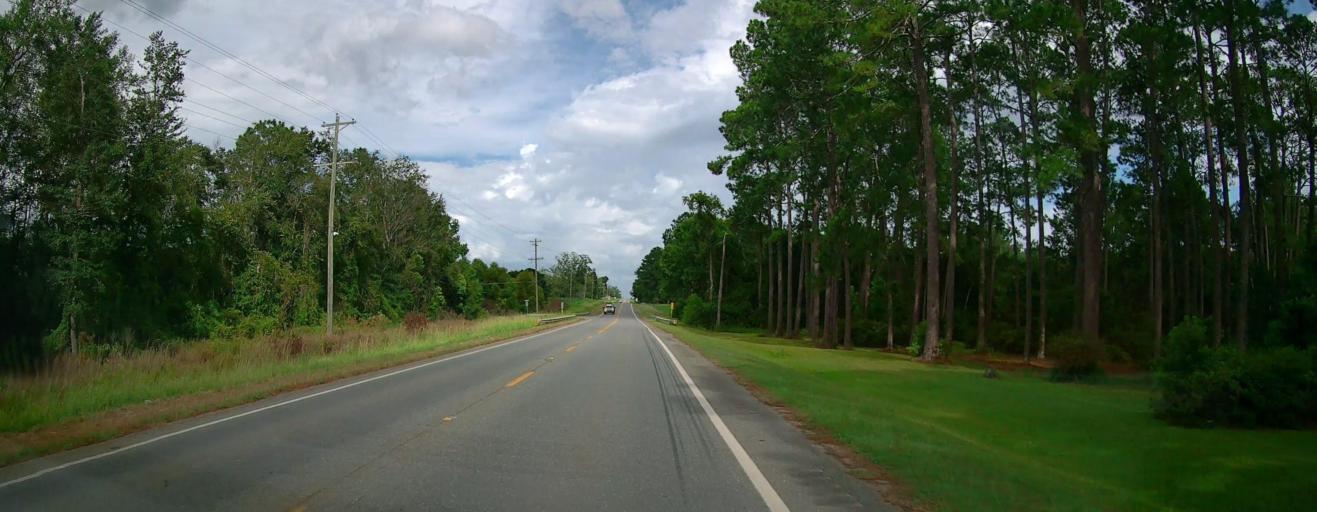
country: US
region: Georgia
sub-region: Coffee County
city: Douglas
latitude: 31.5383
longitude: -82.8676
